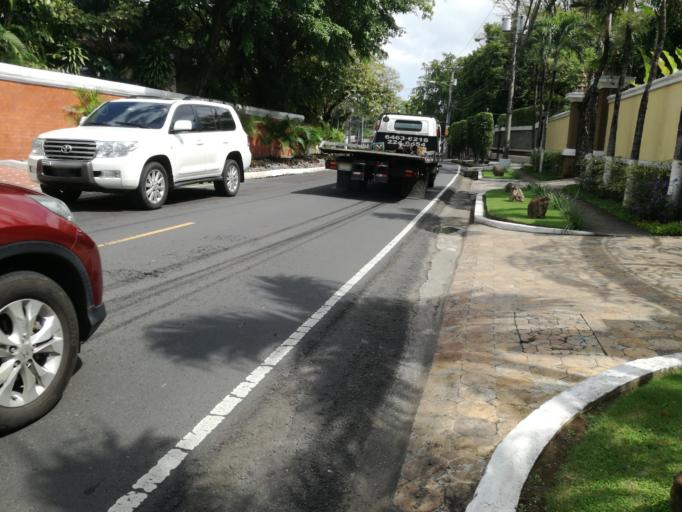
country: PA
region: Panama
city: Panama
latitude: 9.0003
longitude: -79.5026
